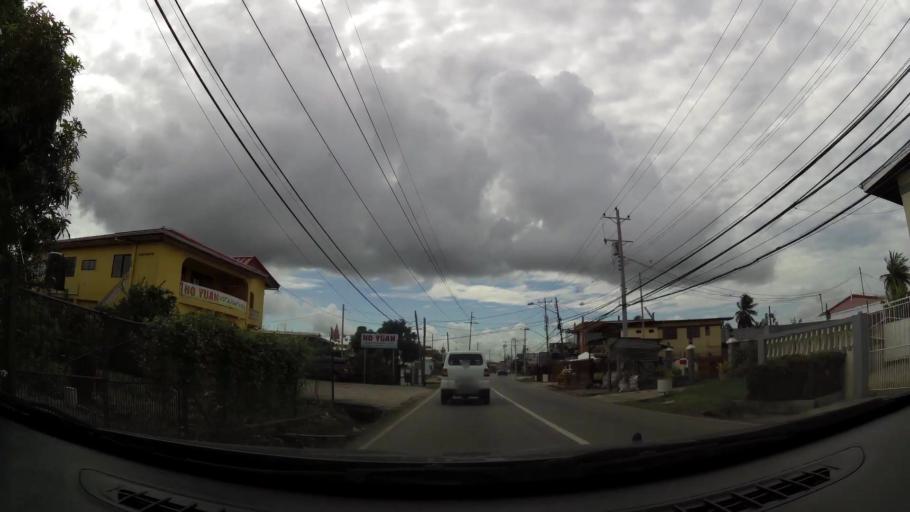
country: TT
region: Chaguanas
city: Chaguanas
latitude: 10.5006
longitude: -61.4079
